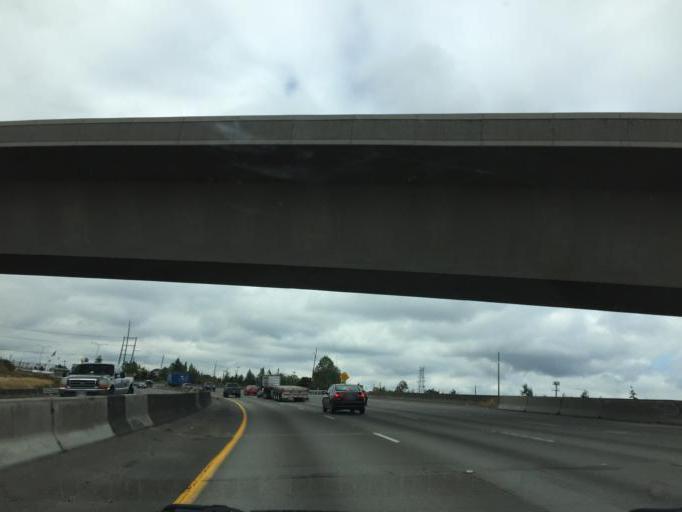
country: US
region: Washington
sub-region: Pierce County
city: Tacoma
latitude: 47.2306
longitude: -122.4604
